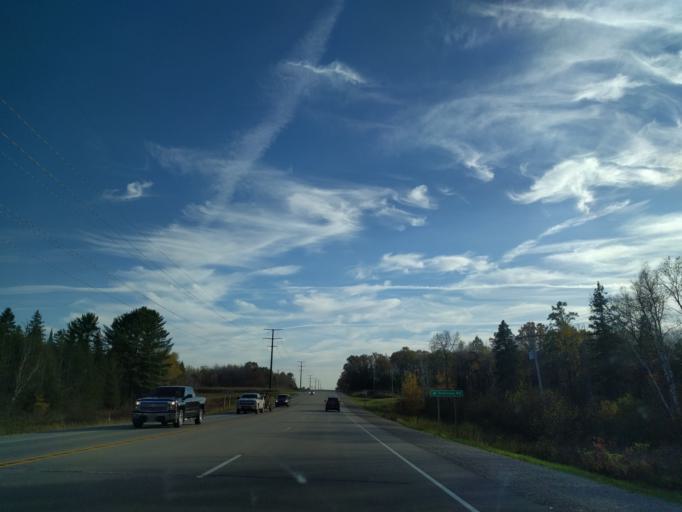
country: US
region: Wisconsin
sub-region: Marinette County
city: Peshtigo
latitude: 45.2818
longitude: -87.9909
